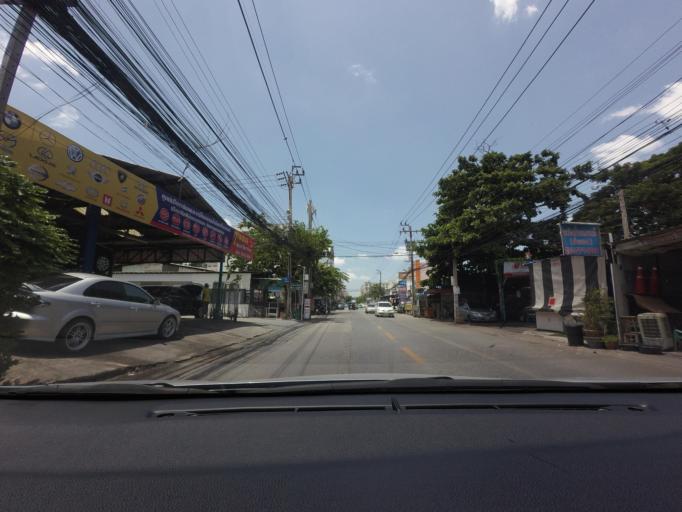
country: TH
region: Bangkok
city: Bang Na
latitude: 13.6970
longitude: 100.6380
